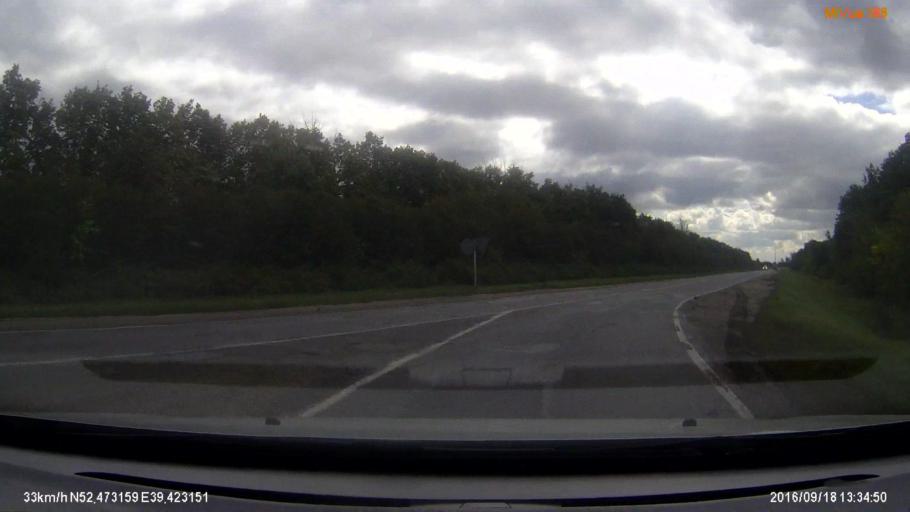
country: RU
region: Lipetsk
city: Borinskoye
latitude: 52.4920
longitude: 39.4470
